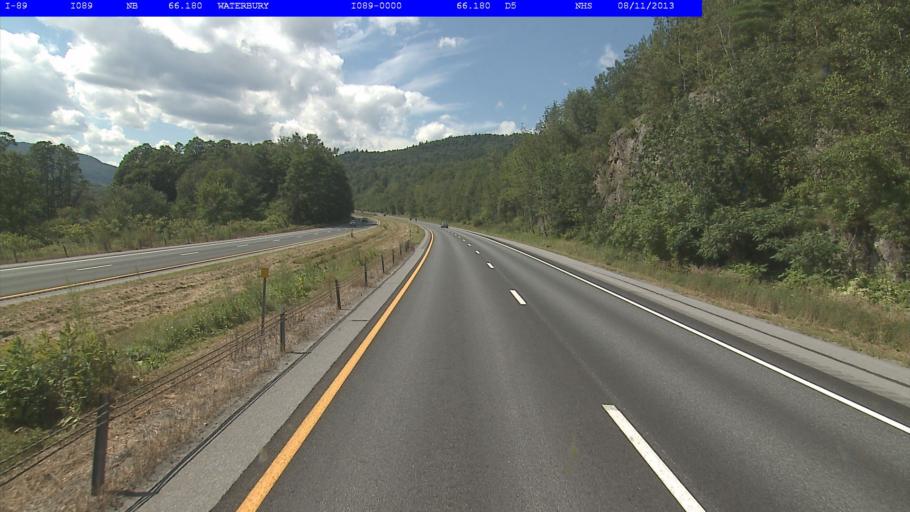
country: US
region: Vermont
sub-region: Washington County
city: Waterbury
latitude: 44.3589
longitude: -72.7948
